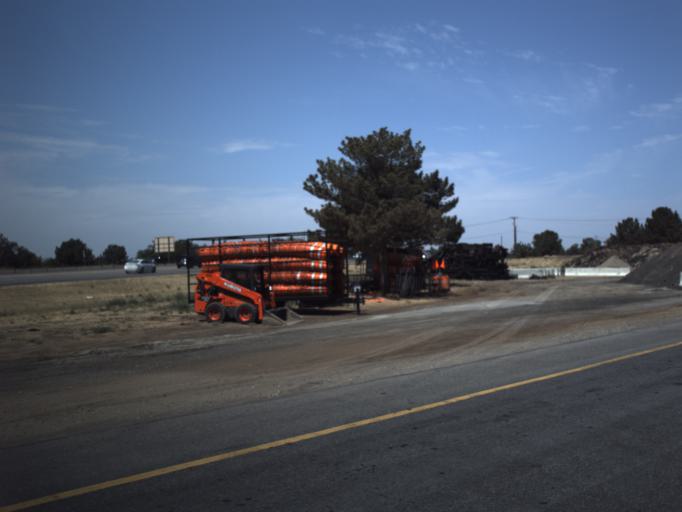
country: US
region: Utah
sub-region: Davis County
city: Hill Air Force Bace
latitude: 41.1017
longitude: -112.0014
